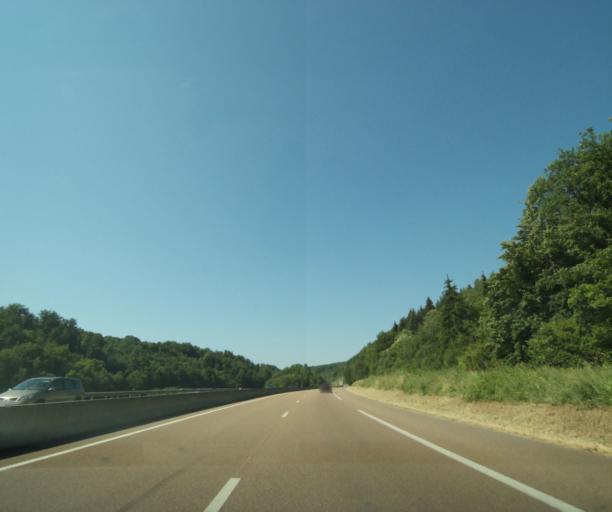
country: FR
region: Lorraine
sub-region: Departement de la Meuse
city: Ligny-en-Barrois
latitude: 48.6864
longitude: 5.3136
